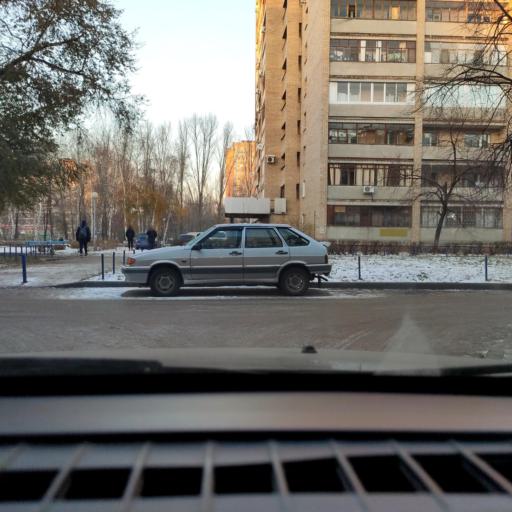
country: RU
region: Samara
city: Tol'yatti
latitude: 53.5319
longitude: 49.2893
